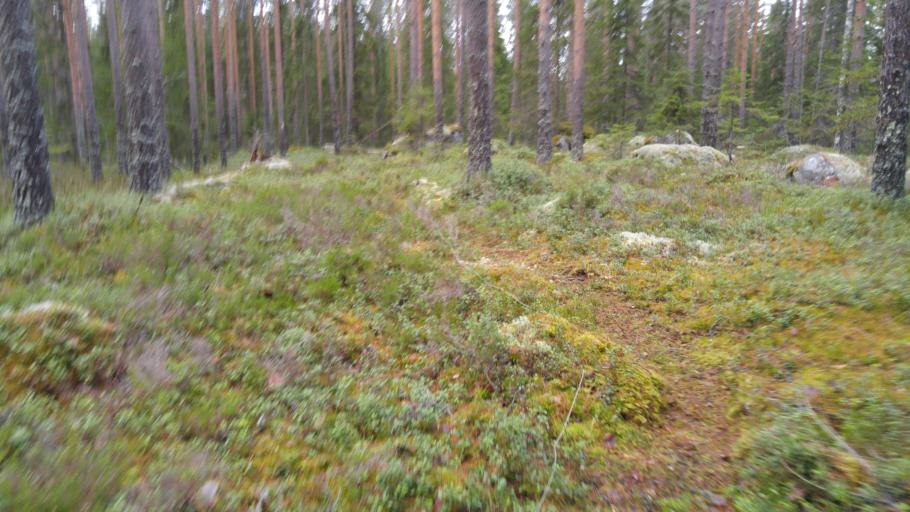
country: FI
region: Pirkanmaa
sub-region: Tampere
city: Kangasala
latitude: 61.6066
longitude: 23.9796
